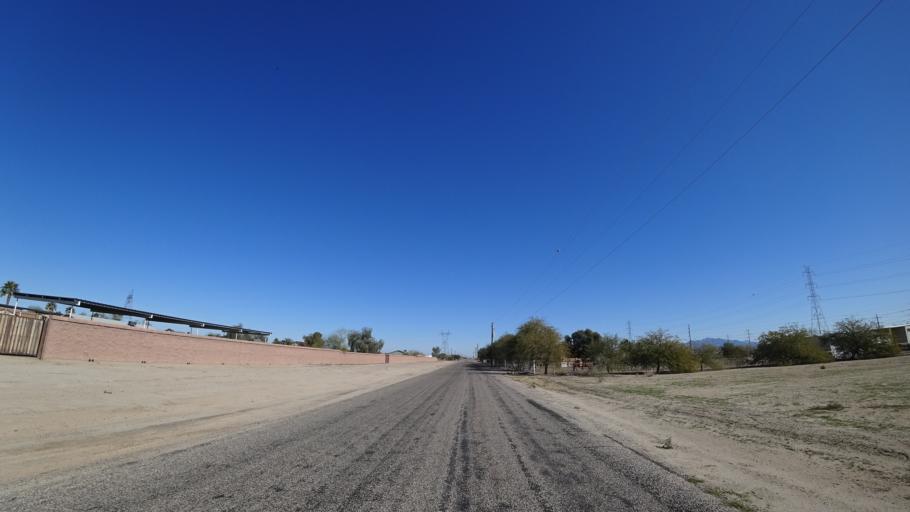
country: US
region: Arizona
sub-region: Maricopa County
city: Buckeye
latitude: 33.4212
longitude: -112.5333
